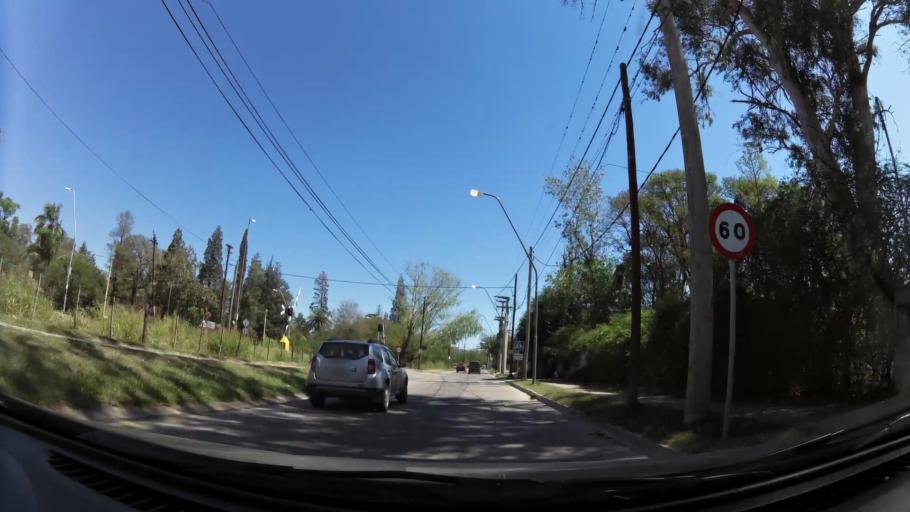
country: AR
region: Cordoba
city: Saldan
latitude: -31.3372
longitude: -64.2838
